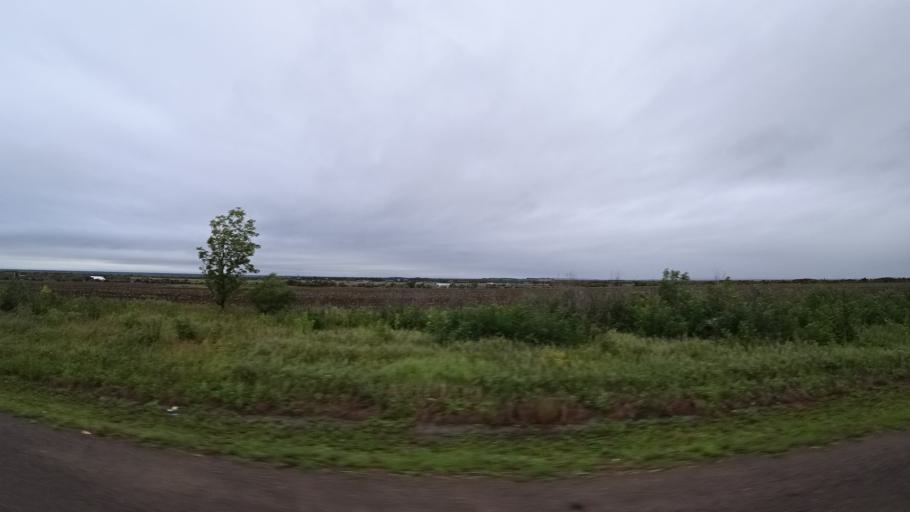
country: RU
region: Primorskiy
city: Chernigovka
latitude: 44.3147
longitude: 132.5568
